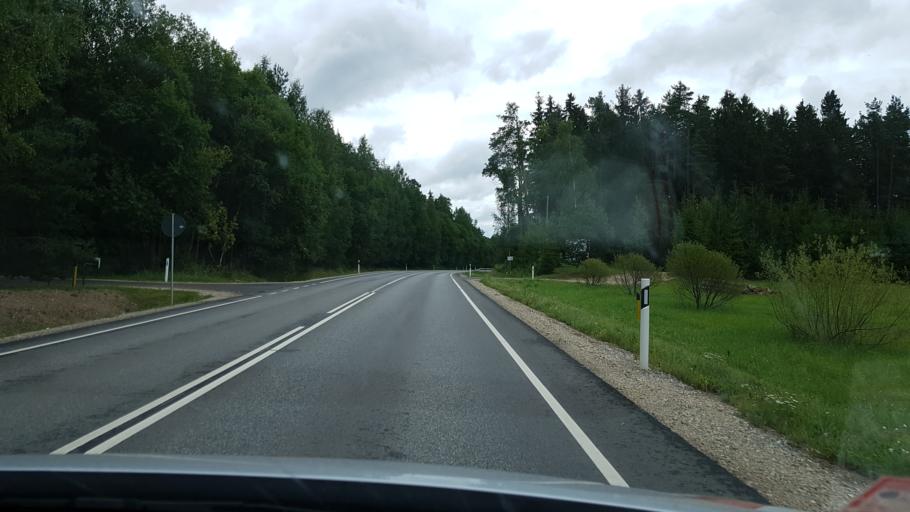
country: EE
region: Polvamaa
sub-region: Polva linn
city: Polva
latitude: 58.0240
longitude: 27.1611
